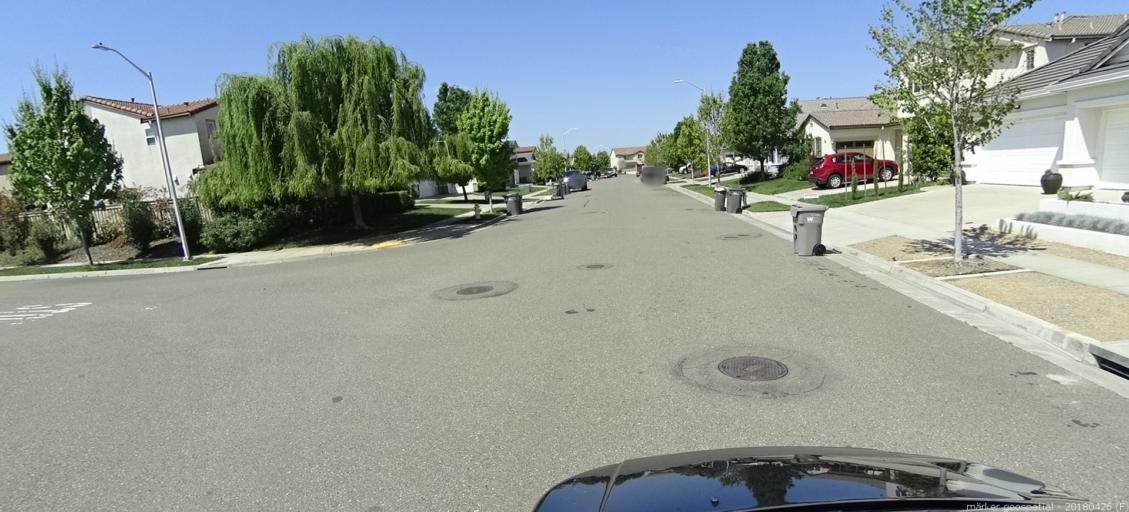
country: US
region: California
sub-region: Yolo County
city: West Sacramento
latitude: 38.5297
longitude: -121.5736
